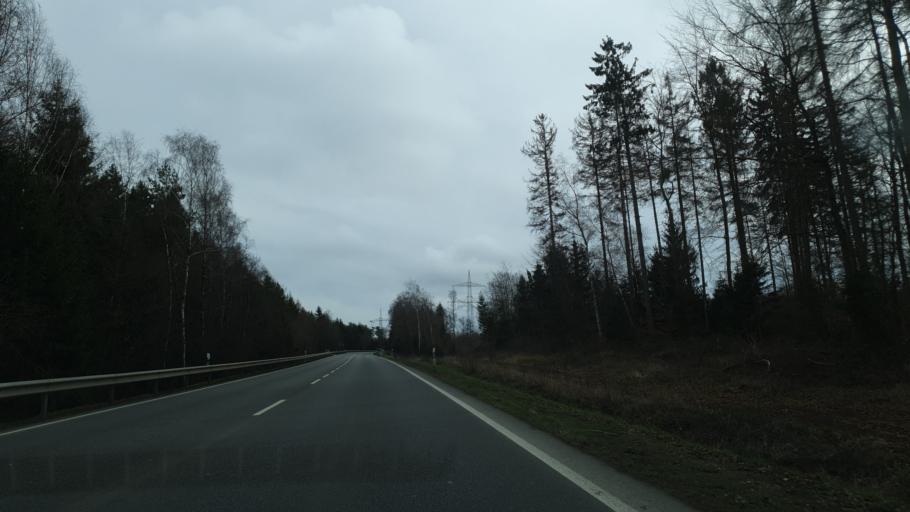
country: DE
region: Rheinland-Pfalz
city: Emmelshausen
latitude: 50.1628
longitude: 7.5714
